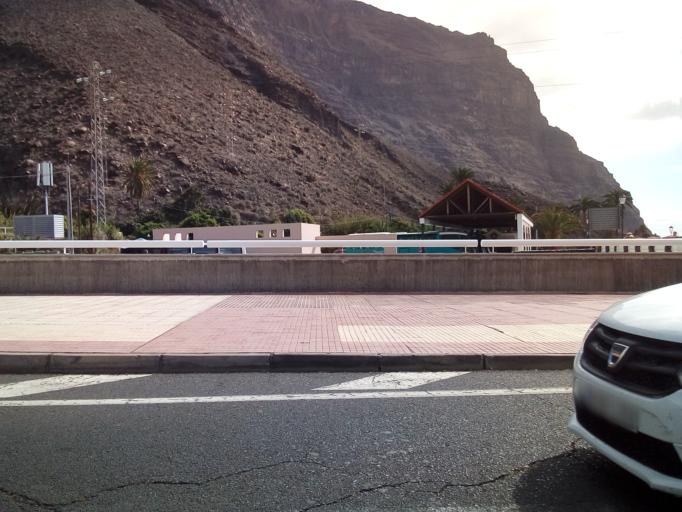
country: ES
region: Canary Islands
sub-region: Provincia de Santa Cruz de Tenerife
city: Alajero
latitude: 28.0943
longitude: -17.3358
